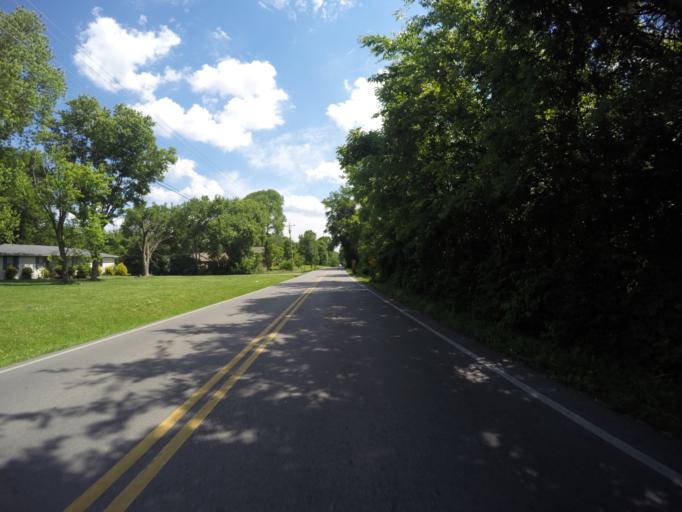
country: US
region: Tennessee
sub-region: Wilson County
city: Green Hill
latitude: 36.2200
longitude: -86.5497
